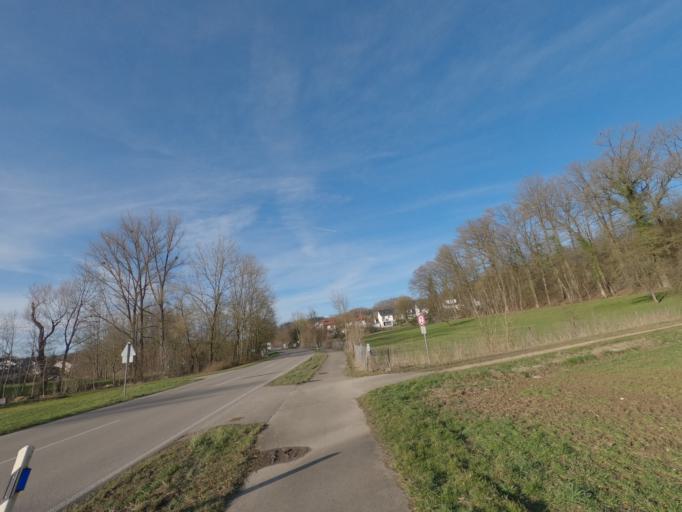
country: DE
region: Baden-Wuerttemberg
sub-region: Regierungsbezirk Stuttgart
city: Donzdorf
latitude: 48.7040
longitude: 9.7984
